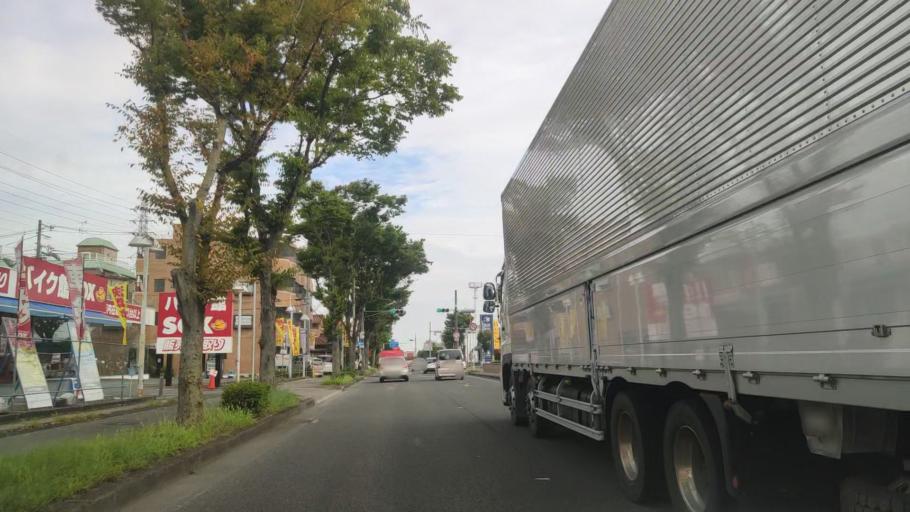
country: JP
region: Osaka
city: Tondabayashicho
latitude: 34.5241
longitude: 135.6050
